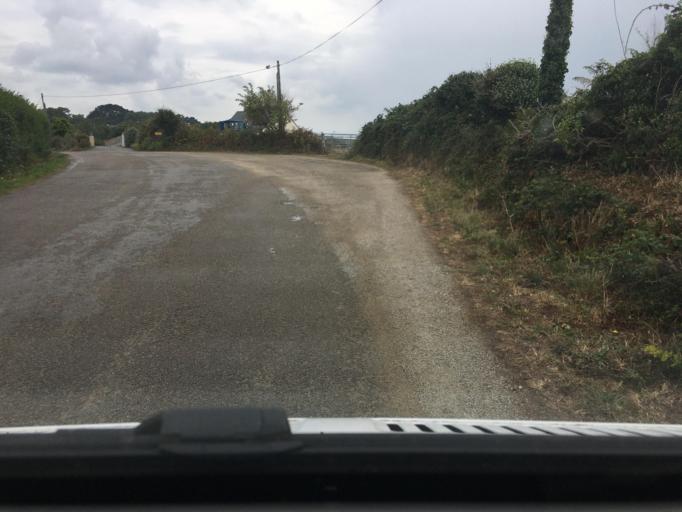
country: FR
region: Brittany
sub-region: Departement du Finistere
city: Beuzec-Cap-Sizun
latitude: 48.0843
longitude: -4.4808
